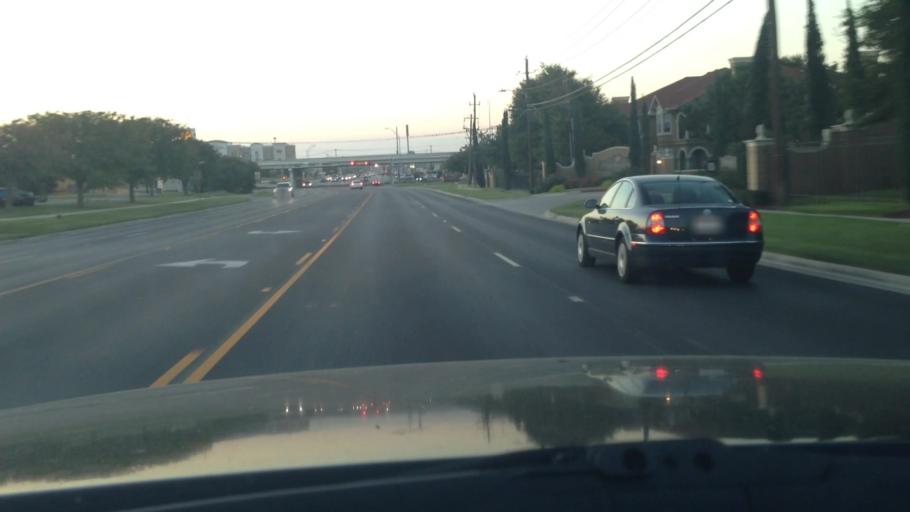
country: US
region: Texas
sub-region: Hays County
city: San Marcos
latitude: 29.8553
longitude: -97.9511
